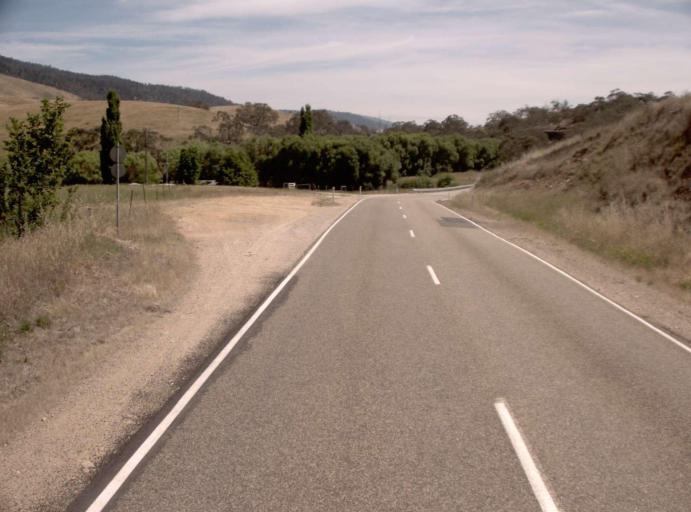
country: AU
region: Victoria
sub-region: Alpine
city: Mount Beauty
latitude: -37.0680
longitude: 147.6031
